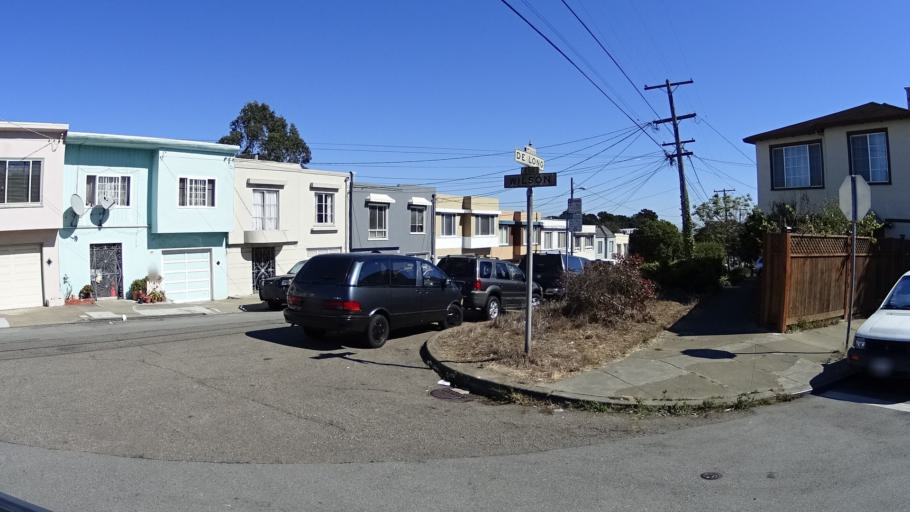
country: US
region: California
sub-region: San Mateo County
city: Daly City
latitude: 37.7096
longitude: -122.4618
